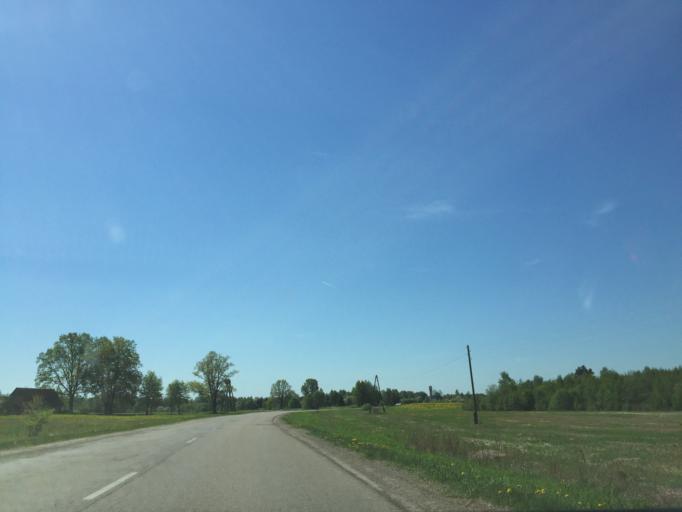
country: LV
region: Malpils
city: Malpils
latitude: 56.9198
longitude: 24.9364
